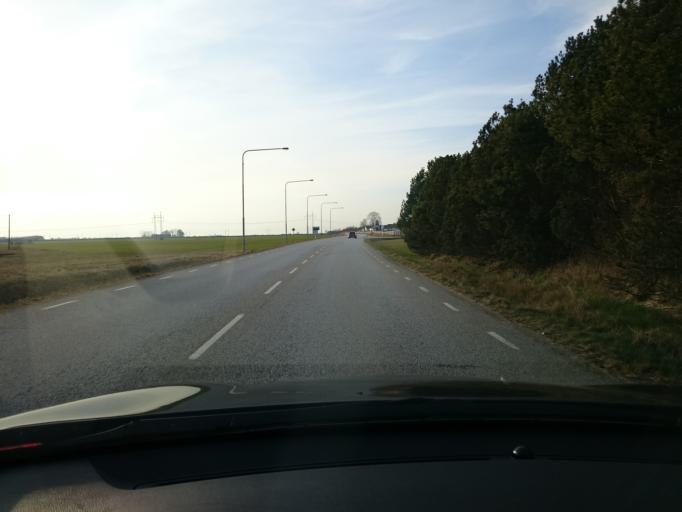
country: SE
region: Skane
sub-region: Staffanstorps Kommun
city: Hjaerup
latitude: 55.6659
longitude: 13.1371
